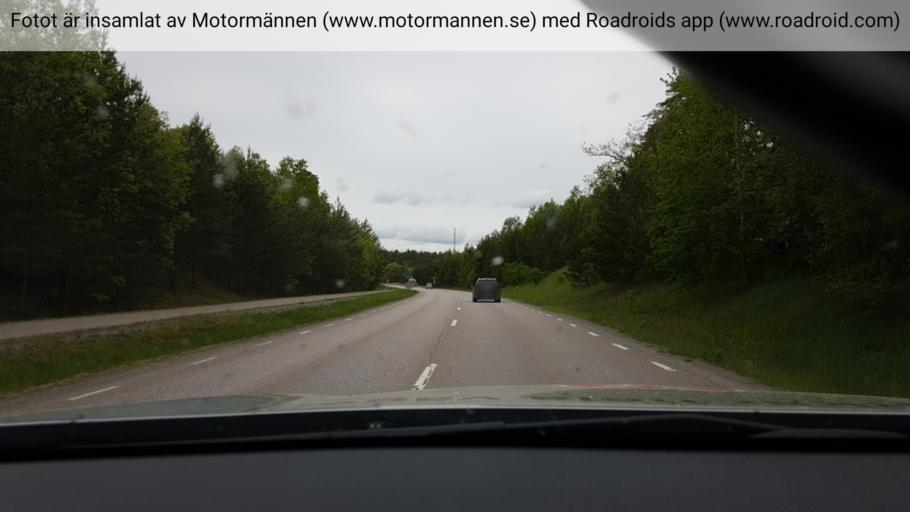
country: SE
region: Stockholm
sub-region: Vaxholms Kommun
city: Vaxholm
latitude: 59.3961
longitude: 18.4256
